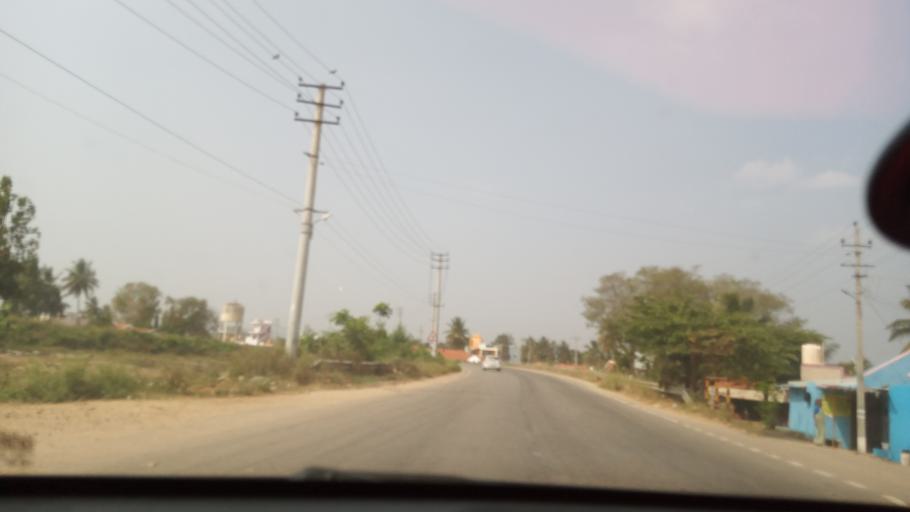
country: IN
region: Karnataka
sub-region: Chamrajnagar
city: Chamrajnagar
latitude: 11.9875
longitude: 76.8714
